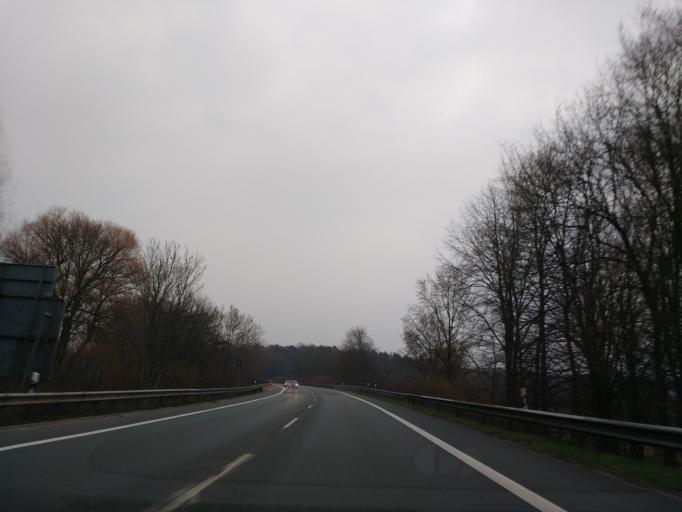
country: DE
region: North Rhine-Westphalia
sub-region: Regierungsbezirk Munster
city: Lotte
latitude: 52.3049
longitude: 7.9322
